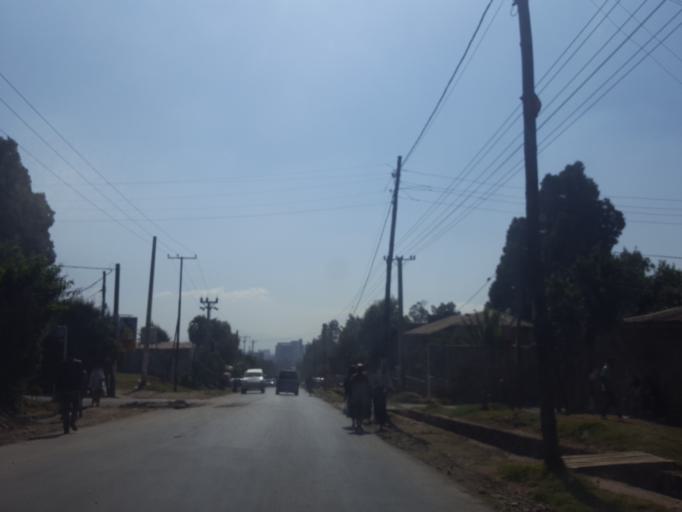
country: ET
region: Adis Abeba
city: Addis Ababa
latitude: 9.0536
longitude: 38.7342
